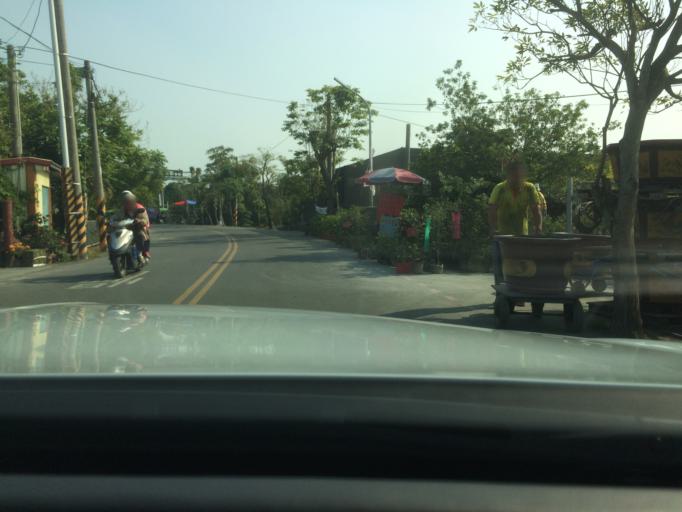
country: TW
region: Taiwan
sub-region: Nantou
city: Nantou
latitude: 23.9026
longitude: 120.5238
